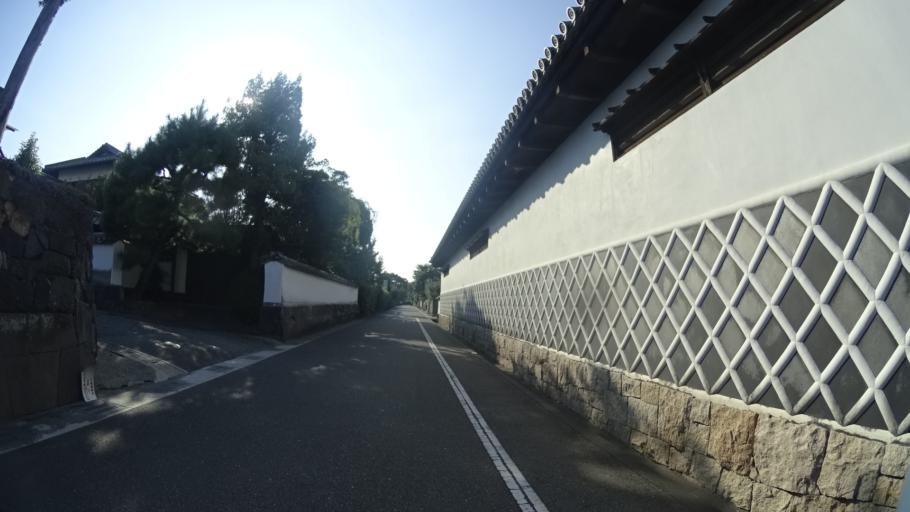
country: JP
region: Yamaguchi
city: Hagi
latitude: 34.4127
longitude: 131.3901
